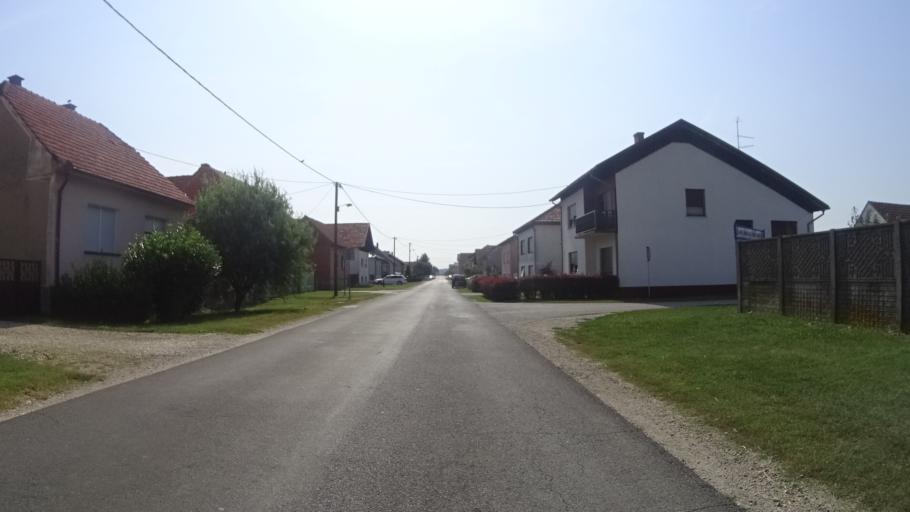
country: HR
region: Medimurska
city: Palovec
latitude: 46.3881
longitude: 16.5440
